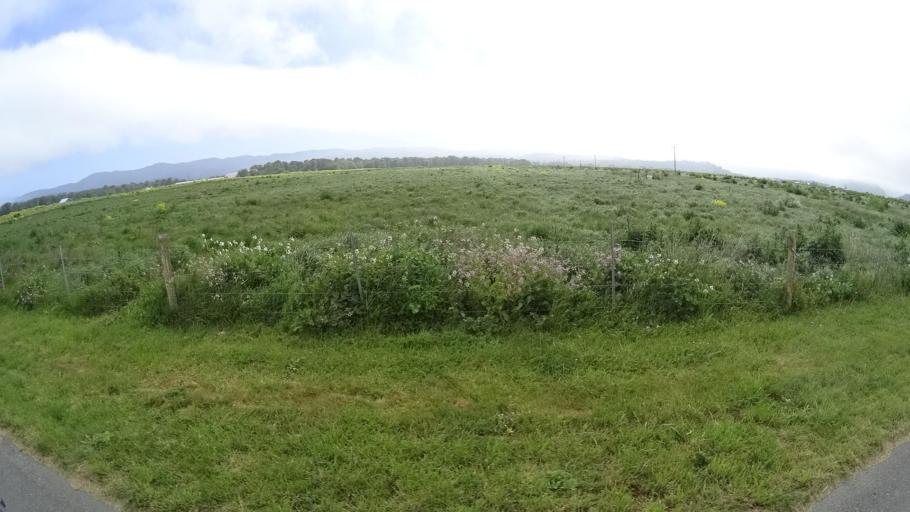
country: US
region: California
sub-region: Humboldt County
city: Fortuna
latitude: 40.5745
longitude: -124.1877
